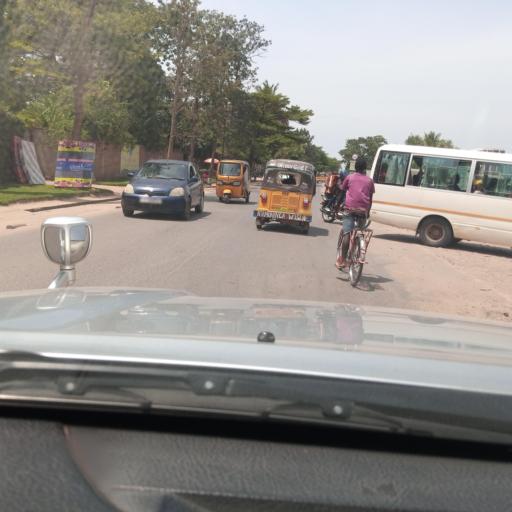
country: BI
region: Bujumbura Mairie
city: Bujumbura
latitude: -3.4074
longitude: 29.3502
